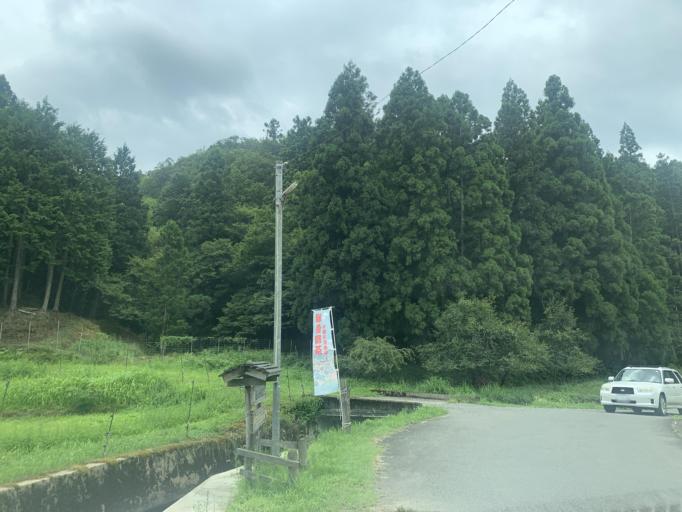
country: JP
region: Kyoto
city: Miyazu
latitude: 35.4449
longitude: 135.1615
